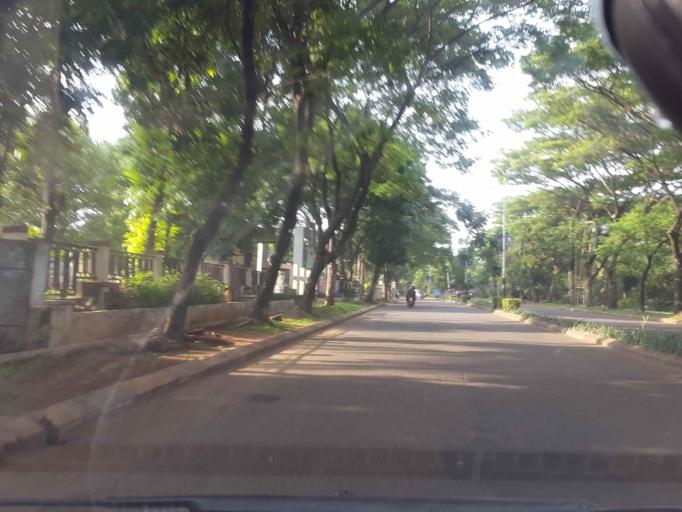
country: ID
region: Banten
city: South Tangerang
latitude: -6.2744
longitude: 106.6935
